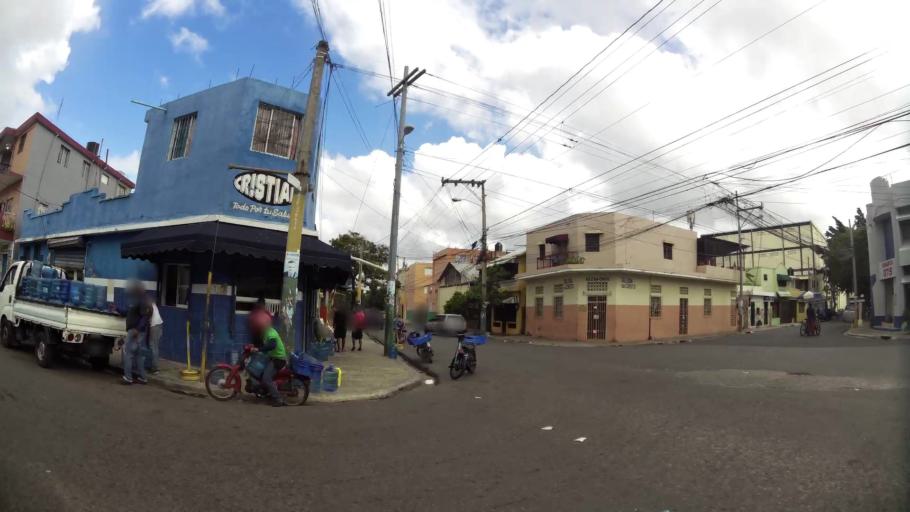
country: DO
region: Nacional
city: San Carlos
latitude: 18.4831
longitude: -69.9035
